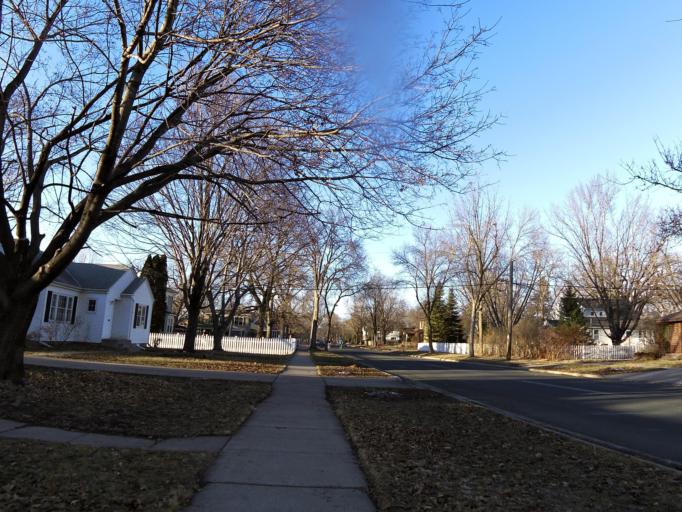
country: US
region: Wisconsin
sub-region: Saint Croix County
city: Hudson
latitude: 44.9783
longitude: -92.7496
